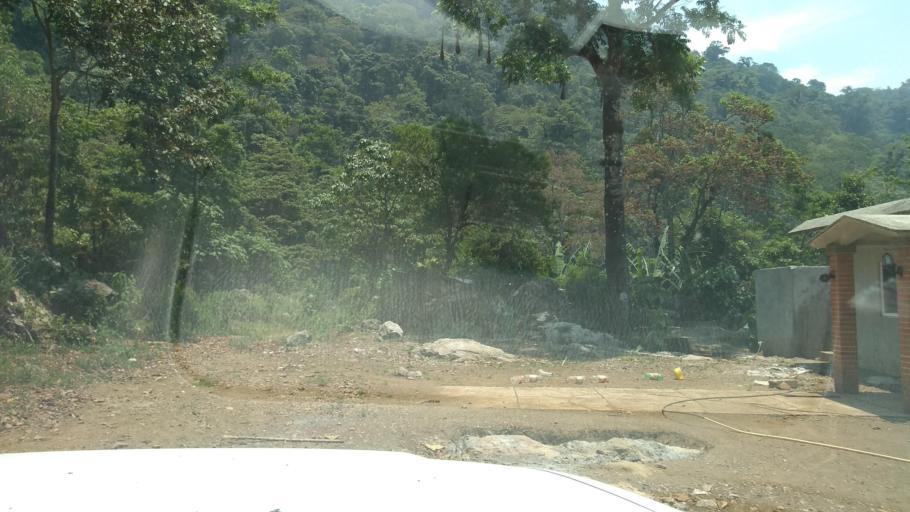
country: MX
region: Veracruz
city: Motzorongo
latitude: 18.6075
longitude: -96.7610
